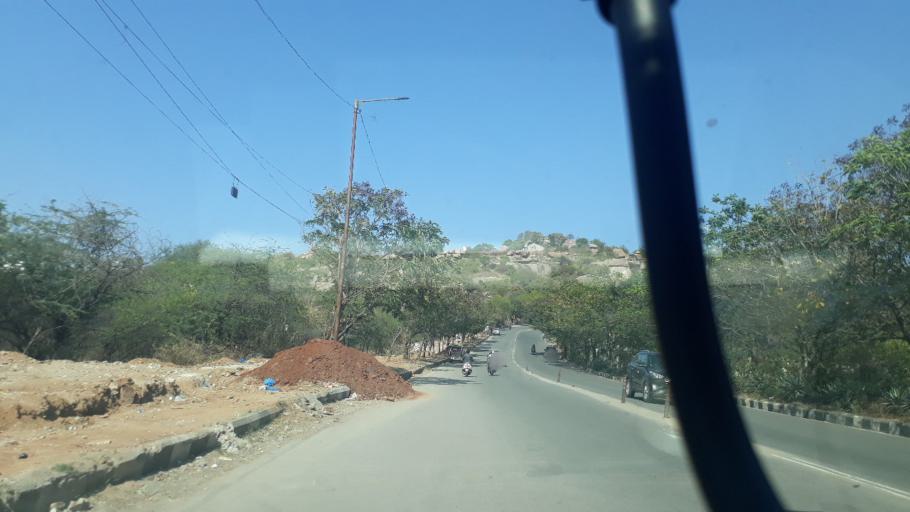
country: IN
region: Telangana
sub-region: Hyderabad
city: Hyderabad
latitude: 17.4162
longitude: 78.3944
